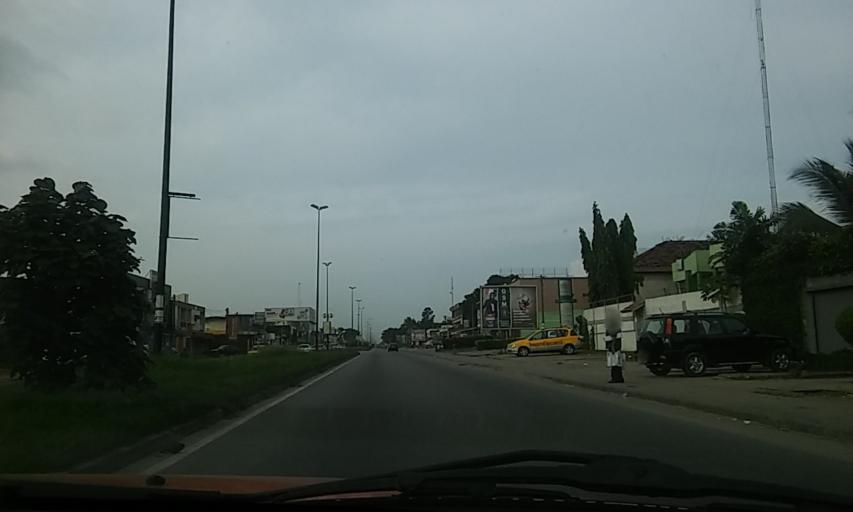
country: CI
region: Lagunes
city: Abobo
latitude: 5.3857
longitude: -3.9930
